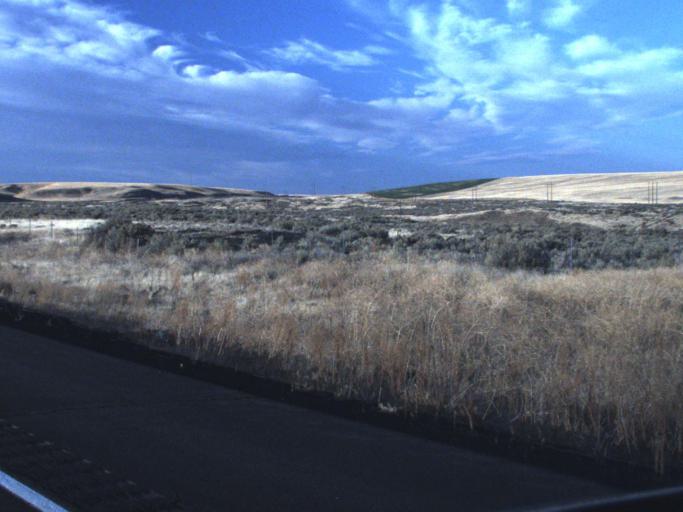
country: US
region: Washington
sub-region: Adams County
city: Ritzville
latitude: 47.0647
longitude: -118.4110
